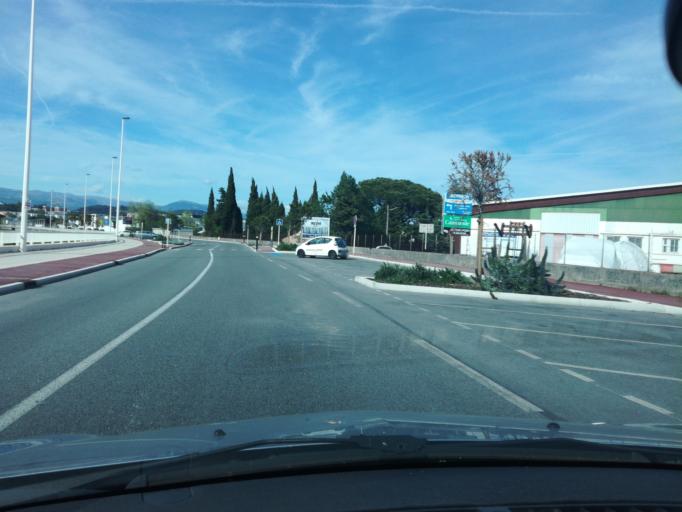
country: FR
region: Provence-Alpes-Cote d'Azur
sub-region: Departement des Alpes-Maritimes
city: Mandelieu-la-Napoule
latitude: 43.5457
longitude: 6.9621
